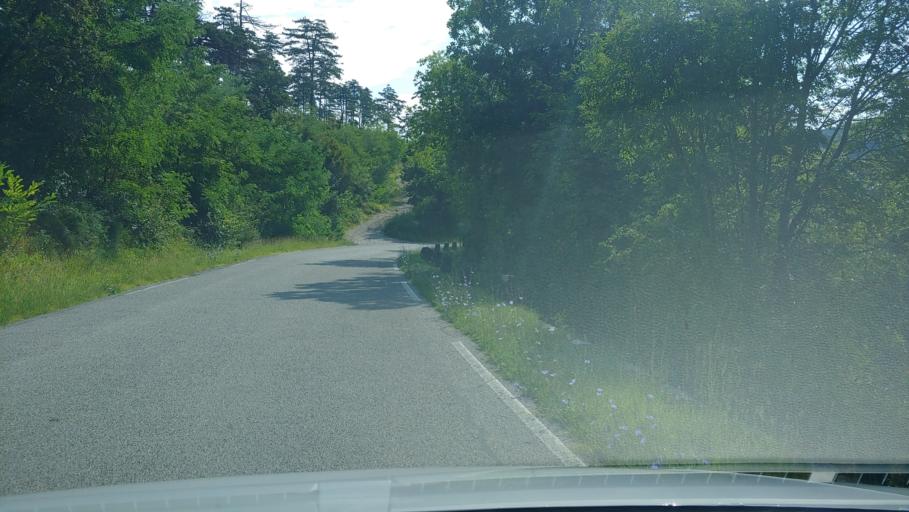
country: SI
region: Komen
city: Komen
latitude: 45.8472
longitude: 13.7834
